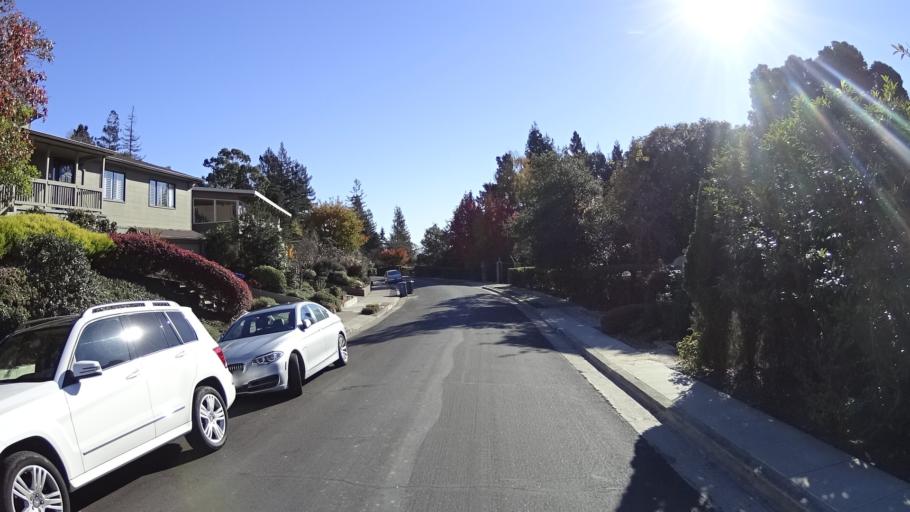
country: US
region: California
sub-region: Alameda County
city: Piedmont
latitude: 37.8212
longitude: -122.2200
